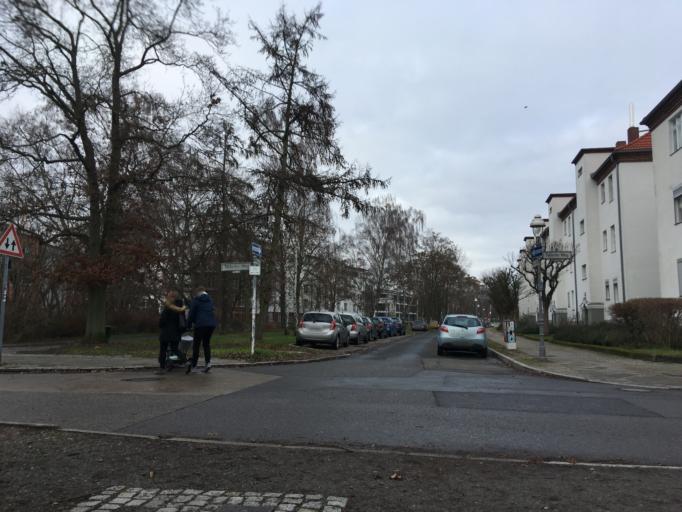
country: DE
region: Berlin
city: Wittenau
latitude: 52.5880
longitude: 13.3297
